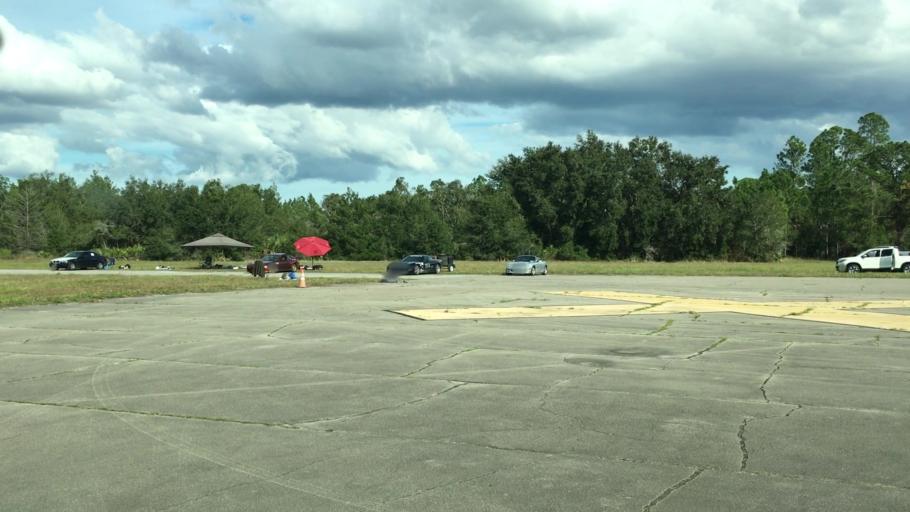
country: US
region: Florida
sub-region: Volusia County
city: North DeLand
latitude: 29.0766
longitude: -81.2871
